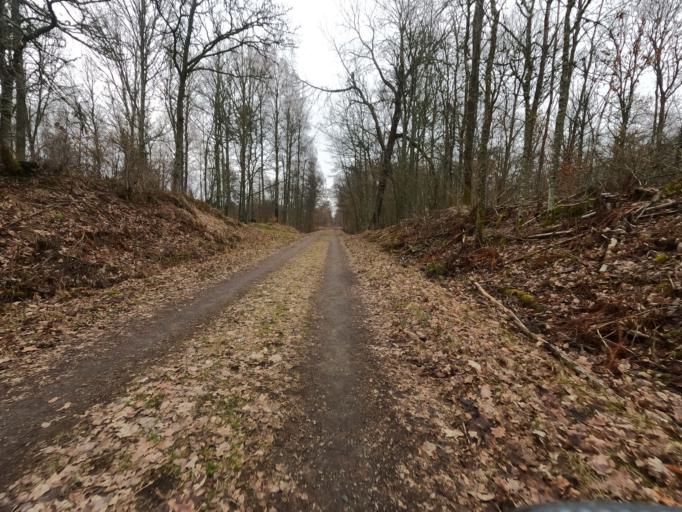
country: SE
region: Kronoberg
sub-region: Markaryds Kommun
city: Stromsnasbruk
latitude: 56.8016
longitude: 13.6780
